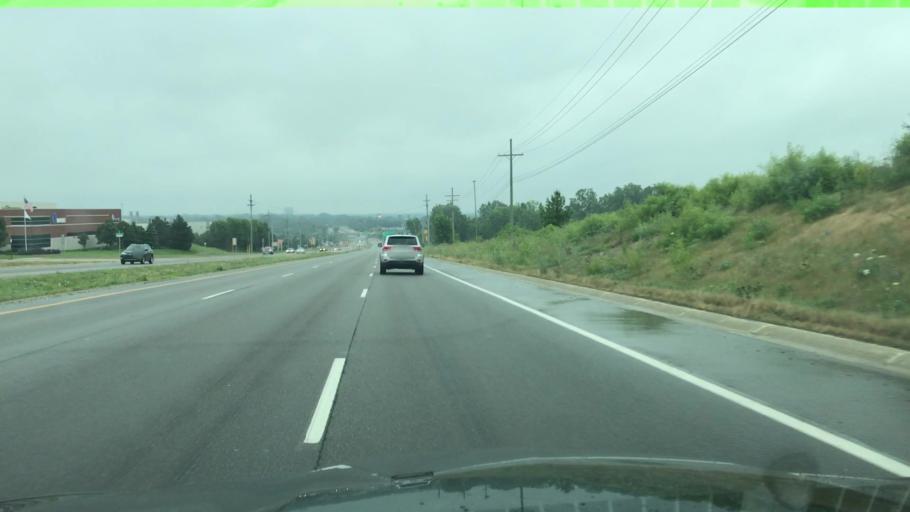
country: US
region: Michigan
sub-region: Oakland County
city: Auburn Hills
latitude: 42.7050
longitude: -83.2427
